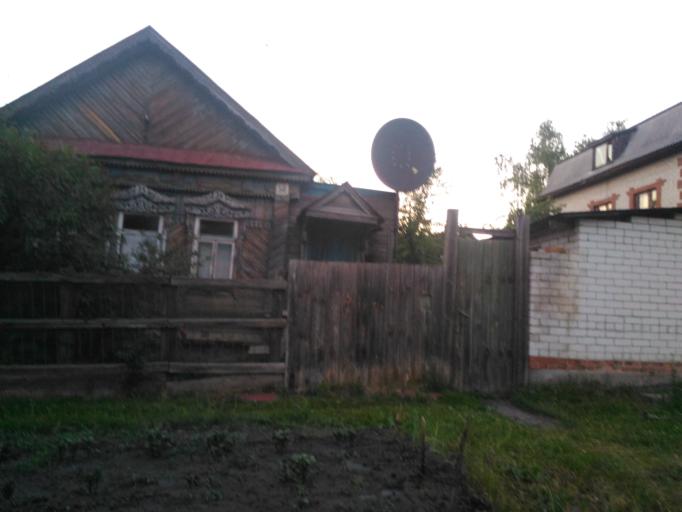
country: RU
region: Ulyanovsk
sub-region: Ulyanovskiy Rayon
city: Ulyanovsk
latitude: 54.3384
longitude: 48.3685
